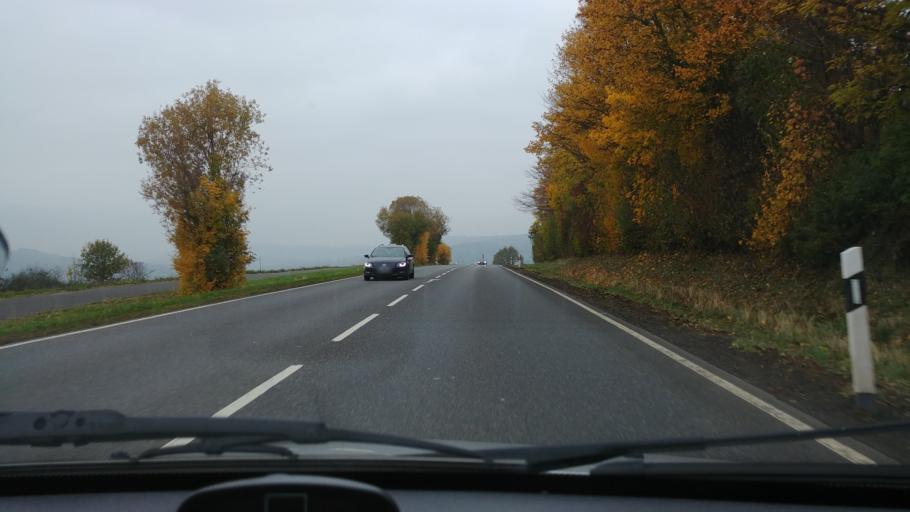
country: DE
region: Hesse
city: Waldbrunn
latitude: 50.4884
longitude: 8.0607
